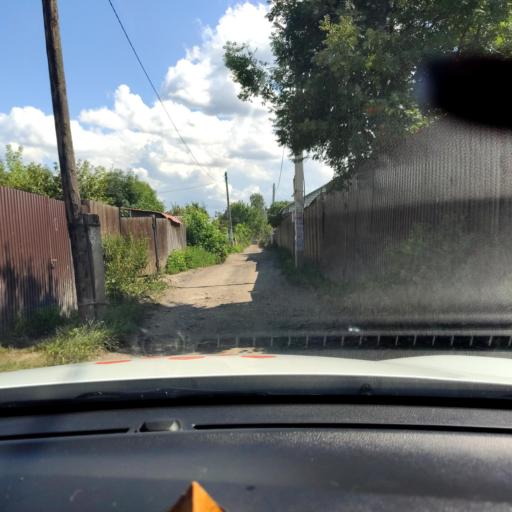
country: RU
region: Tatarstan
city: Osinovo
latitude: 55.8299
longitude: 48.7805
